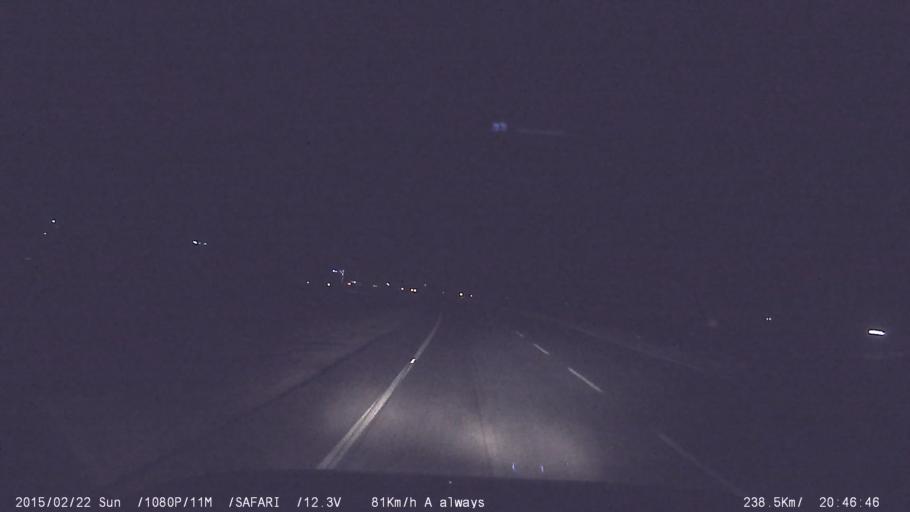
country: IN
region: Tamil Nadu
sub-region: Dindigul
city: Vedasandur
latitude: 10.4863
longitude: 77.9477
